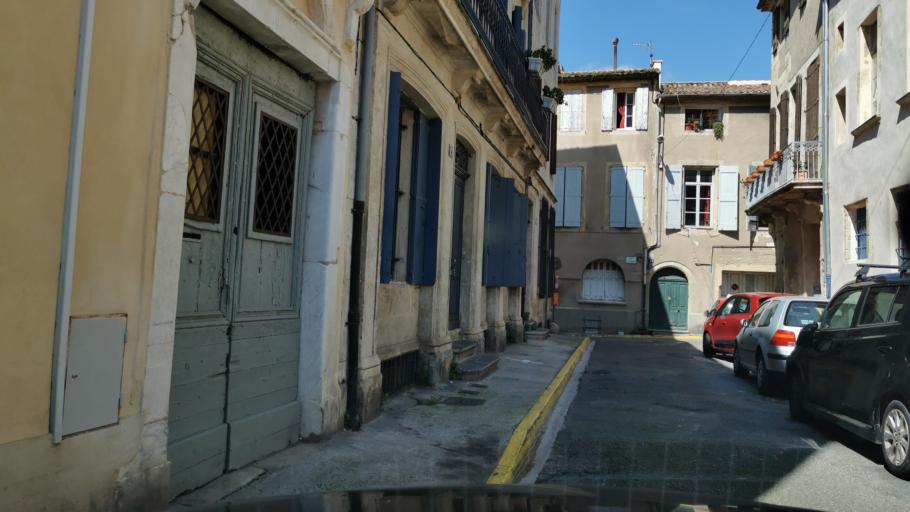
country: FR
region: Languedoc-Roussillon
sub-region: Departement de l'Aude
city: Narbonne
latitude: 43.1841
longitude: 3.0060
